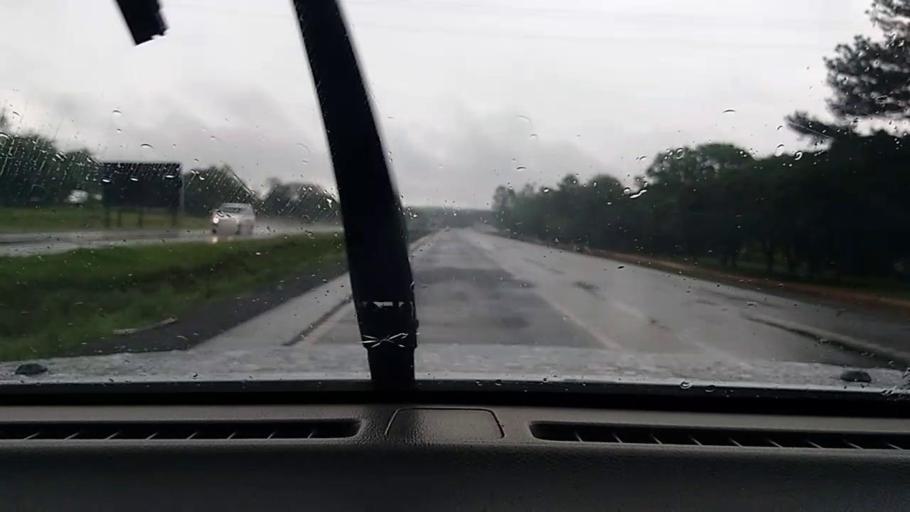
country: PY
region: Caaguazu
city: Repatriacion
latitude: -25.4639
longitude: -55.9300
